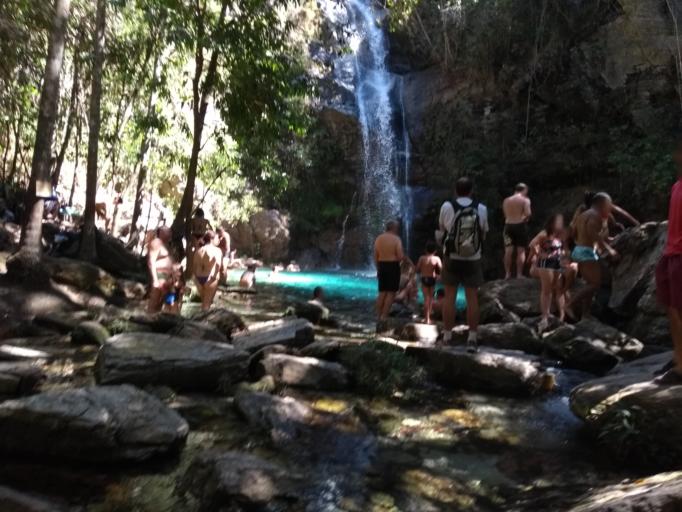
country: BR
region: Goias
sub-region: Cavalcante
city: Cavalcante
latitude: -13.5398
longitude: -47.4925
